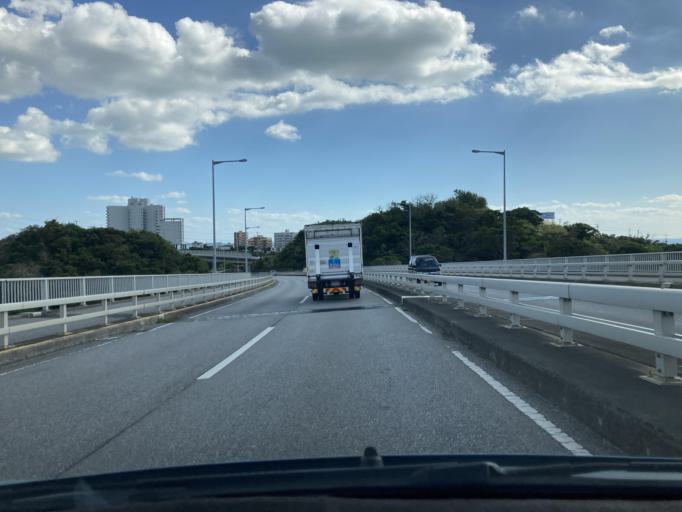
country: JP
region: Okinawa
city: Okinawa
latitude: 26.3147
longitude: 127.8048
